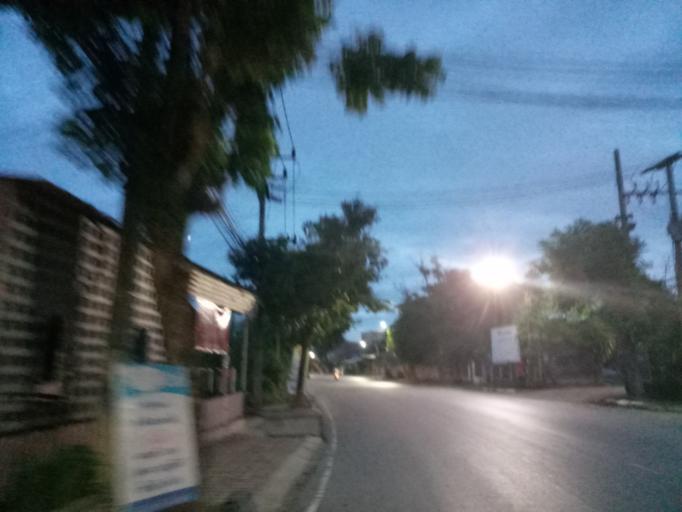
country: TH
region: Chiang Rai
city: Chiang Rai
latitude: 19.8983
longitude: 99.8234
